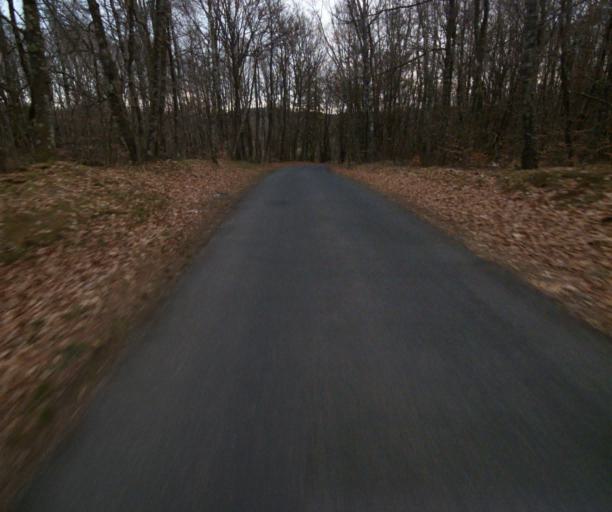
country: FR
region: Limousin
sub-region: Departement de la Correze
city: Correze
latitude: 45.4308
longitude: 1.8414
